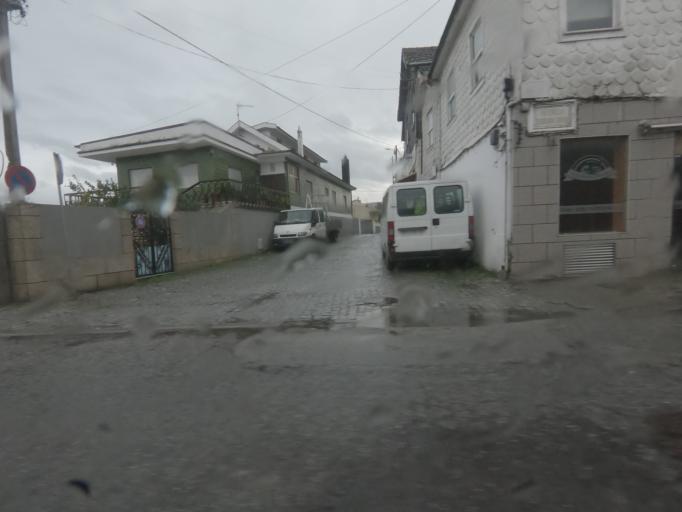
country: PT
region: Vila Real
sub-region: Peso da Regua
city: Godim
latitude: 41.1651
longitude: -7.7973
